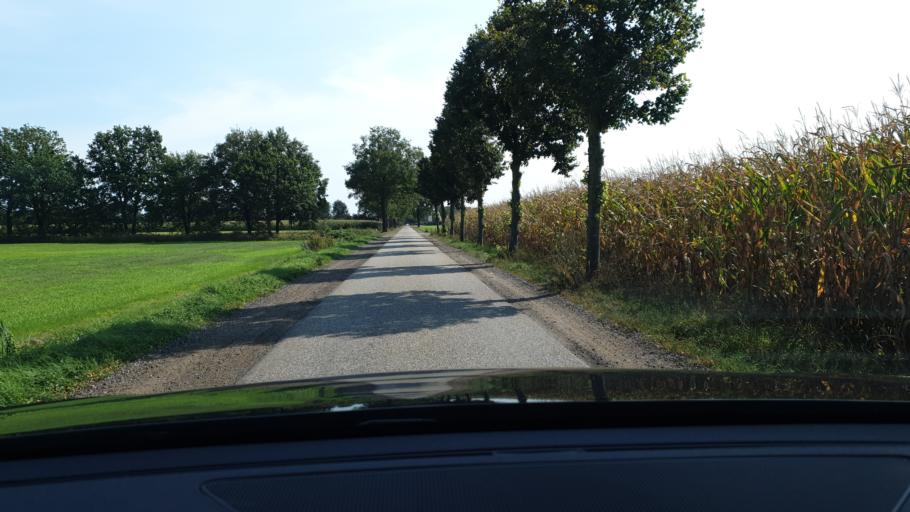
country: NL
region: North Brabant
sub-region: Gemeente Boekel
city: Boekel
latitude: 51.5616
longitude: 5.7359
